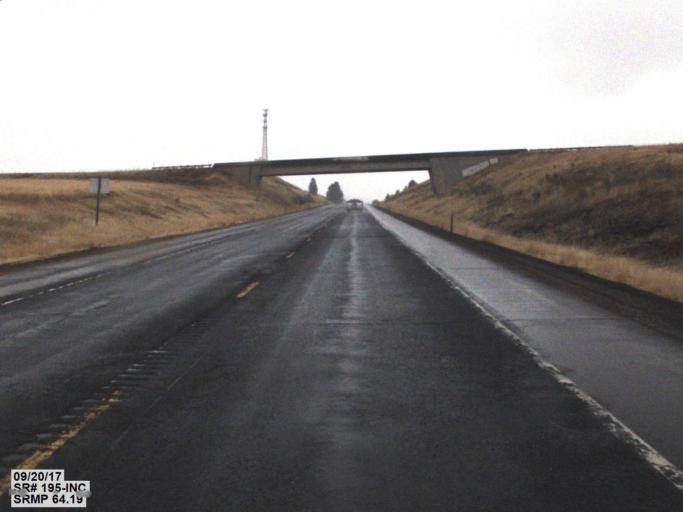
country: US
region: Washington
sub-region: Spokane County
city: Cheney
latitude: 47.2314
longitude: -117.3577
